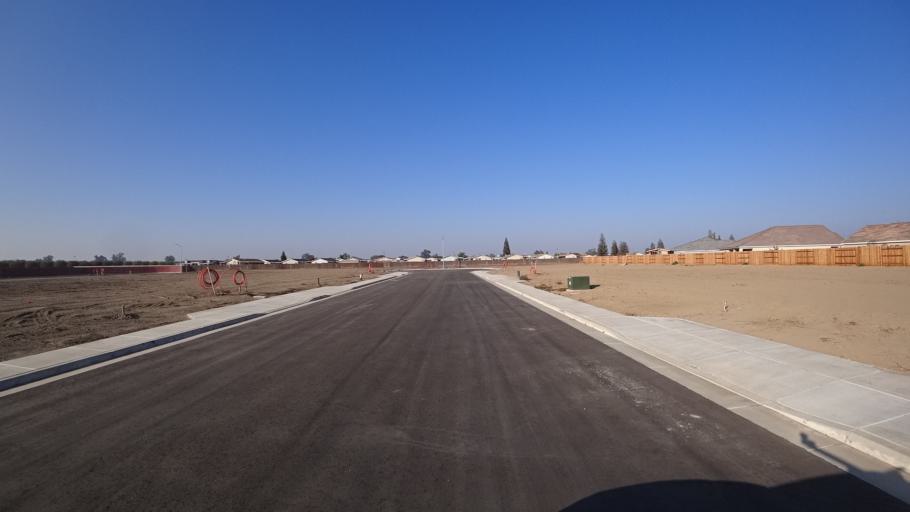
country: US
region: California
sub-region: Kern County
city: Greenfield
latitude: 35.2644
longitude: -119.0140
